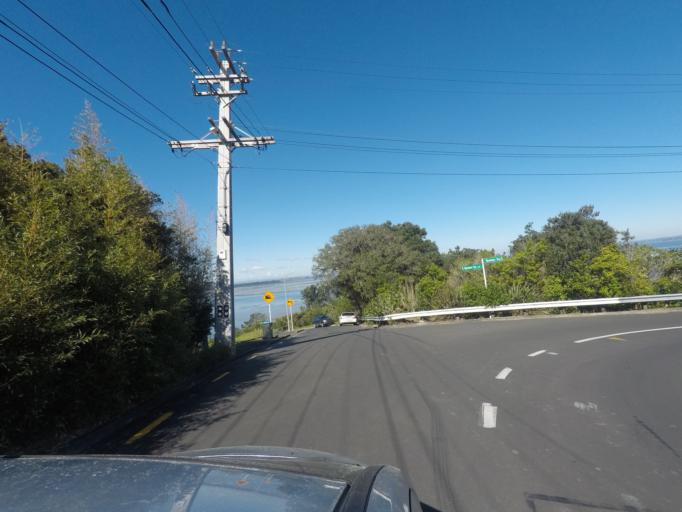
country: NZ
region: Auckland
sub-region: Auckland
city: Titirangi
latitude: -36.9314
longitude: 174.6973
